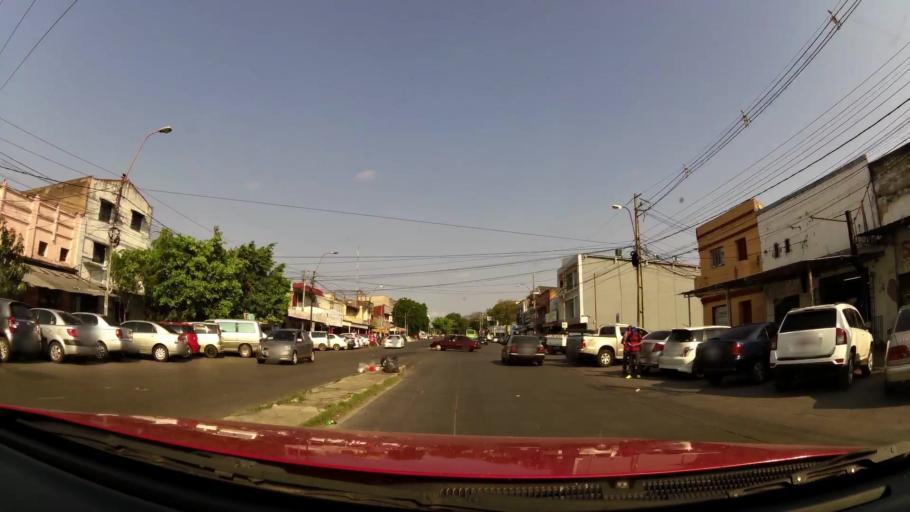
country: PY
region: Asuncion
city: Asuncion
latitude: -25.3001
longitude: -57.6207
